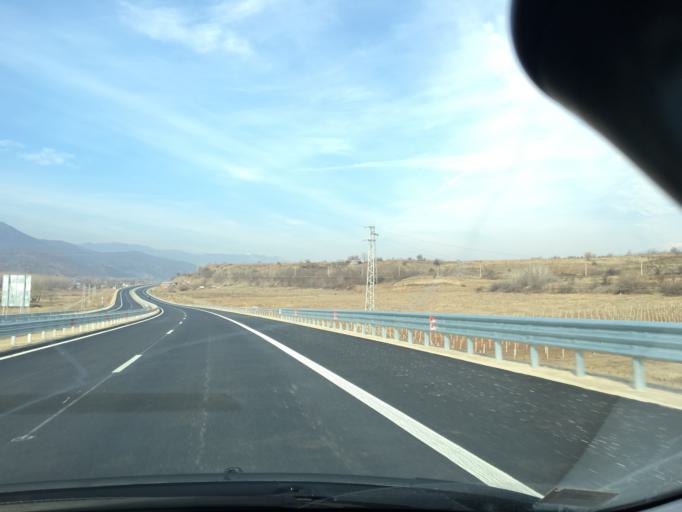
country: BG
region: Blagoevgrad
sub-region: Obshtina Sandanski
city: Sandanski
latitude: 41.5534
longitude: 23.2492
